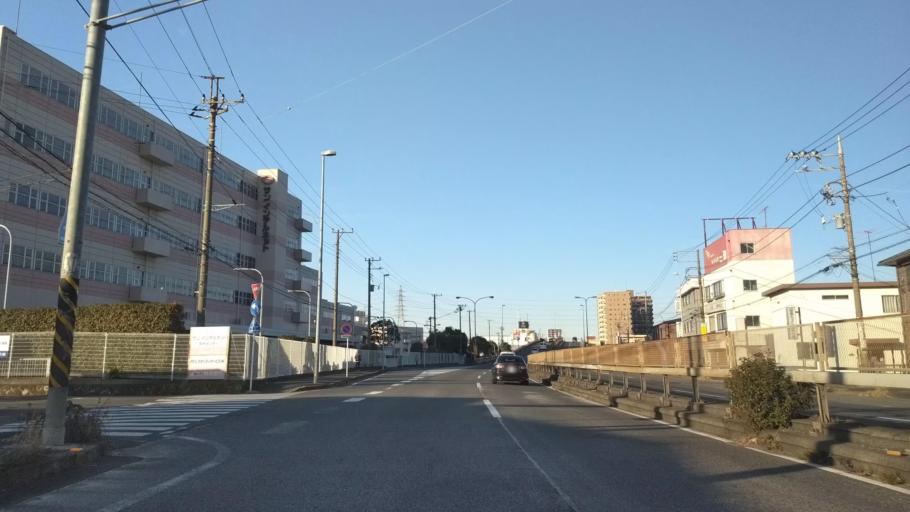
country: JP
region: Kanagawa
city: Atsugi
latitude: 35.4292
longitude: 139.3566
